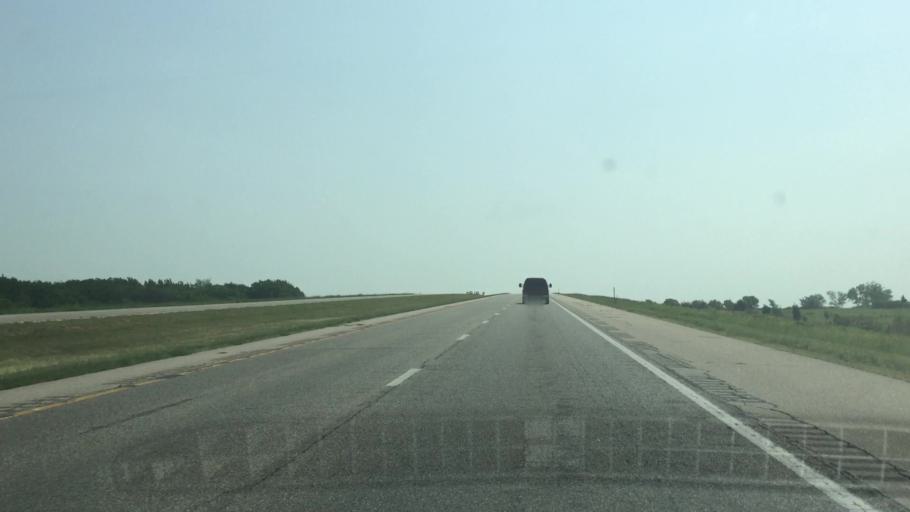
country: US
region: Kansas
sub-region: Osage County
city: Osage City
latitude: 38.4260
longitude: -95.8394
